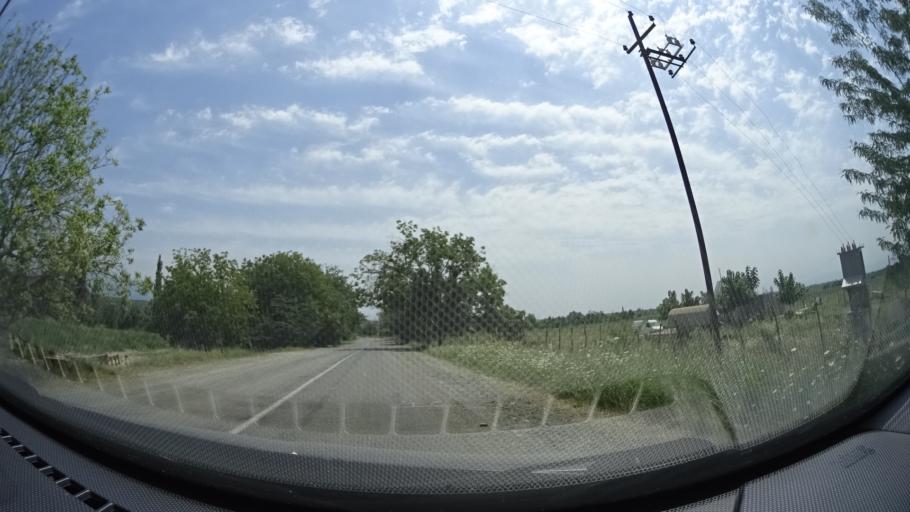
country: GE
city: Bagdadi
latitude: 41.8473
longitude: 46.0584
